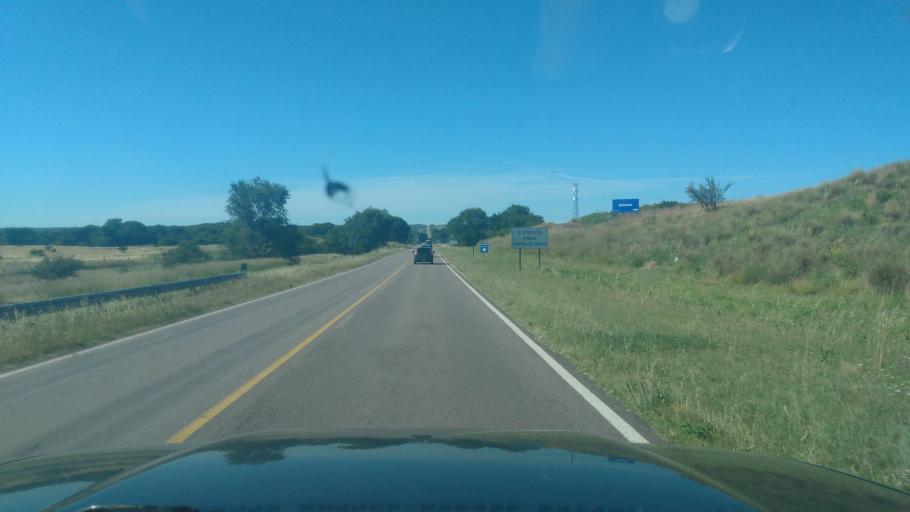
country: AR
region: La Pampa
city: Doblas
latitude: -37.2997
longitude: -64.2878
